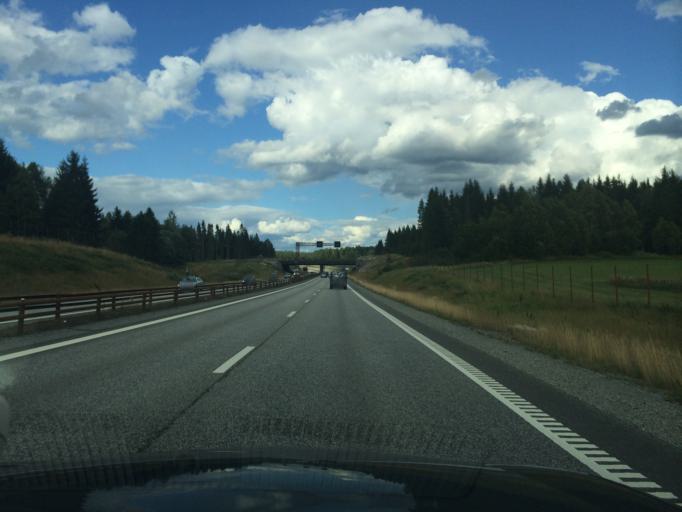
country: NO
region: Akershus
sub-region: Eidsvoll
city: Raholt
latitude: 60.3241
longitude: 11.1776
